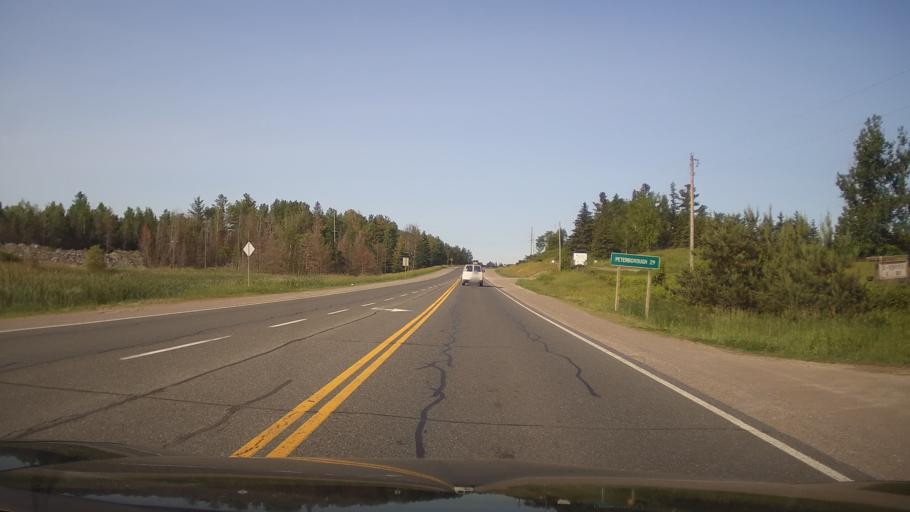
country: CA
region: Ontario
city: Peterborough
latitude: 44.3707
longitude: -77.9922
